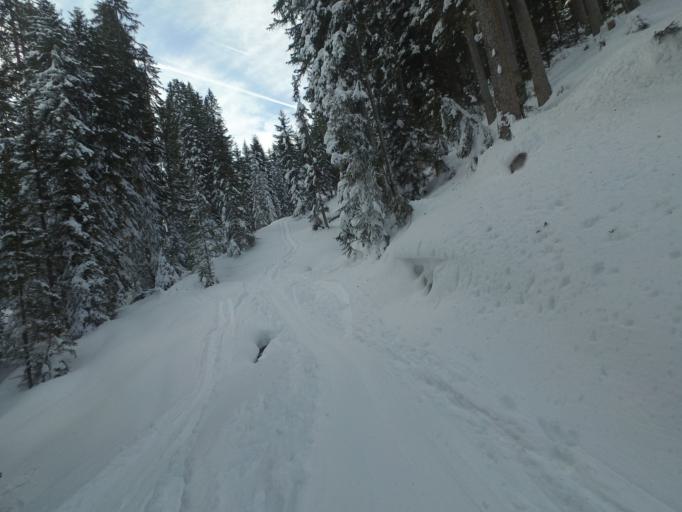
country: AT
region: Salzburg
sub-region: Politischer Bezirk Zell am See
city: Lend
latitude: 47.2753
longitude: 13.0134
